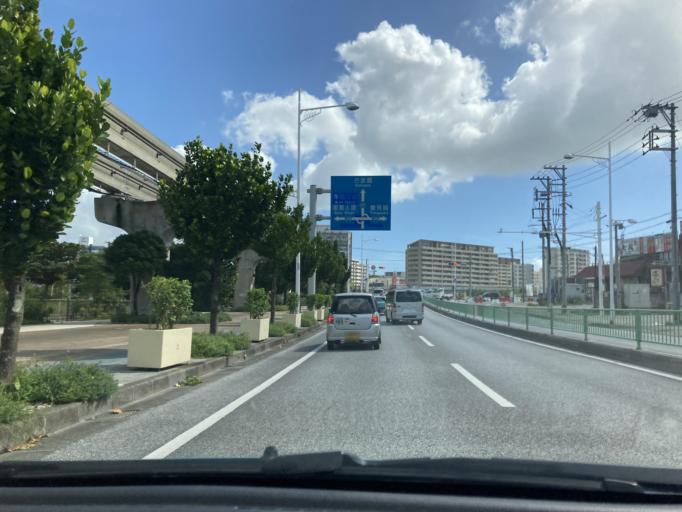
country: JP
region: Okinawa
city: Naha-shi
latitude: 26.2014
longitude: 127.6772
